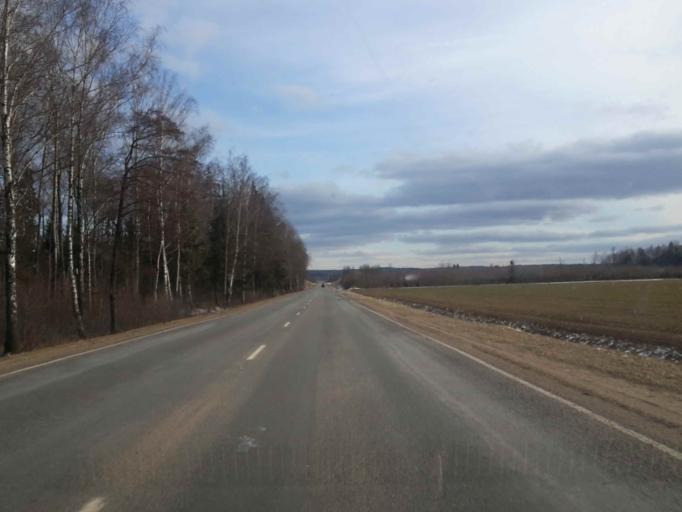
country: BY
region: Minsk
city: Il'ya
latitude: 54.3191
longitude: 27.4683
